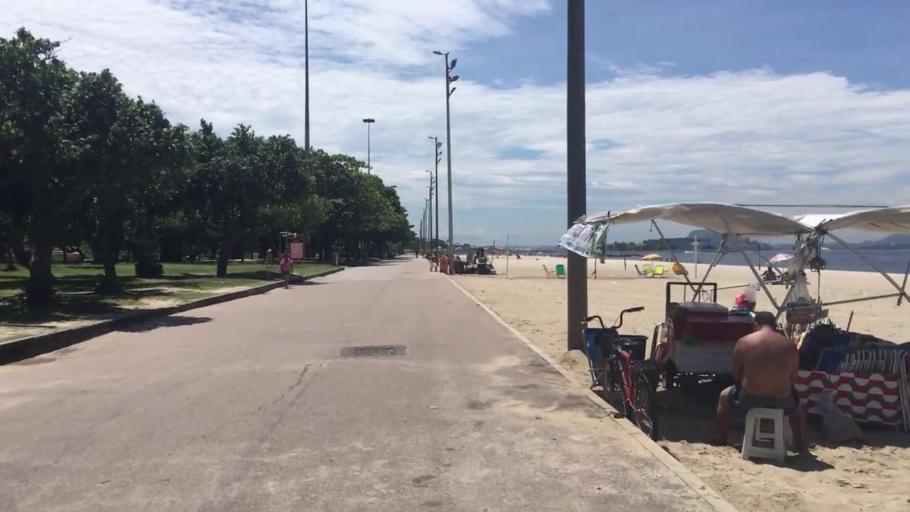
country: BR
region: Rio de Janeiro
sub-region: Rio De Janeiro
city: Rio de Janeiro
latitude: -22.9261
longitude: -43.1702
